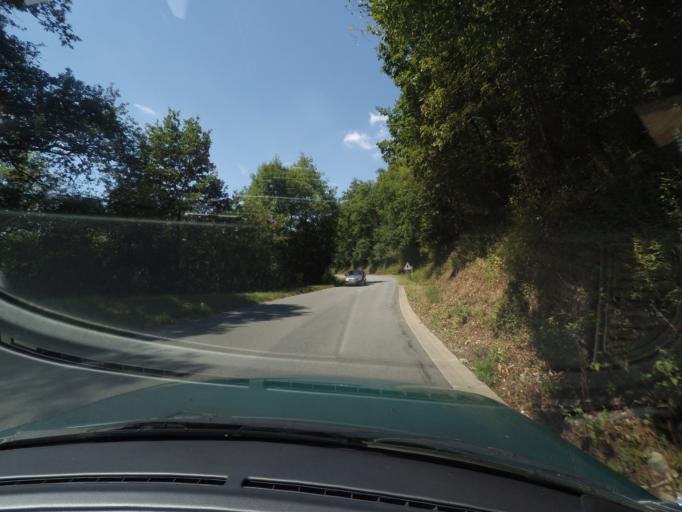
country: FR
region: Limousin
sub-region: Departement de la Haute-Vienne
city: Aixe-sur-Vienne
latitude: 45.7894
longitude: 1.1449
